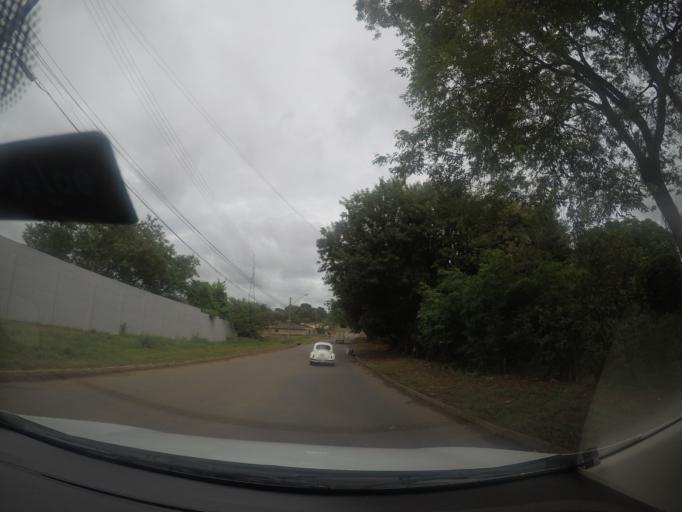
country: BR
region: Goias
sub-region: Goiania
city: Goiania
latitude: -16.6847
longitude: -49.3597
